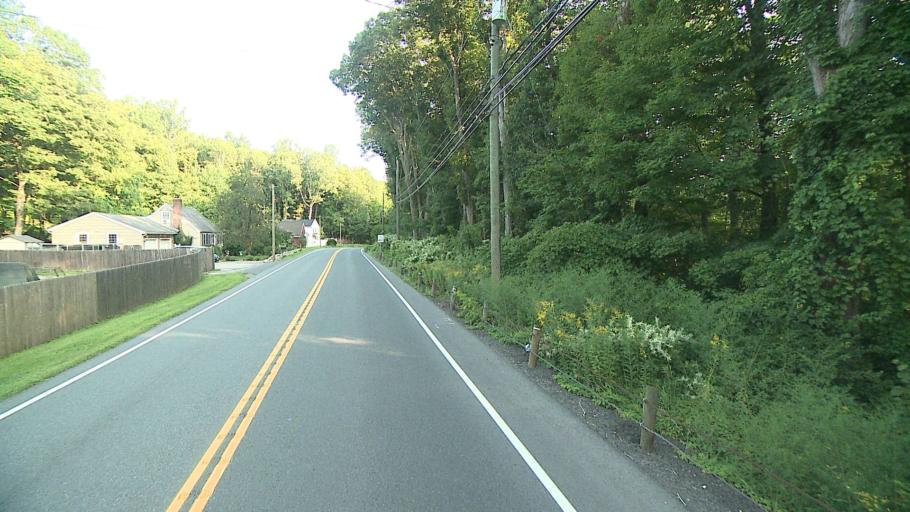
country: US
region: Connecticut
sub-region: Fairfield County
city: Sherman
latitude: 41.5997
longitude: -73.4580
